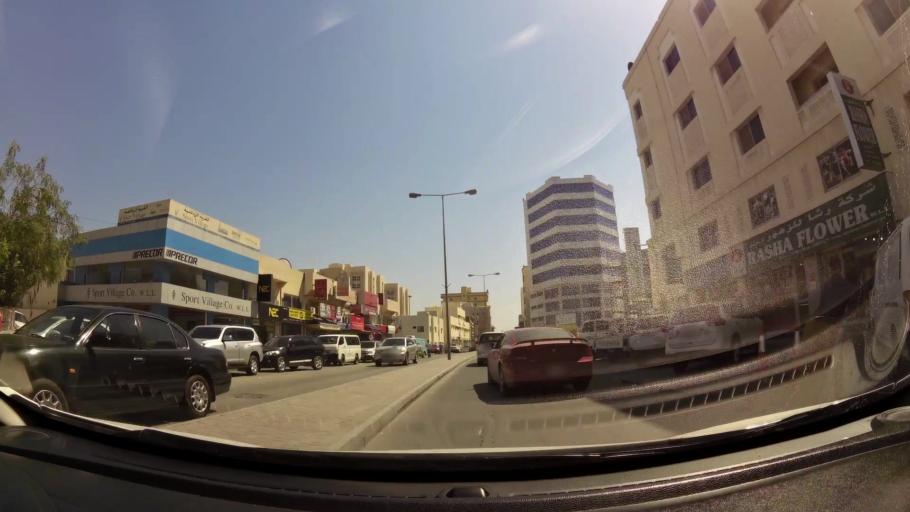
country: BH
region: Manama
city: Manama
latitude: 26.2044
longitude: 50.5964
